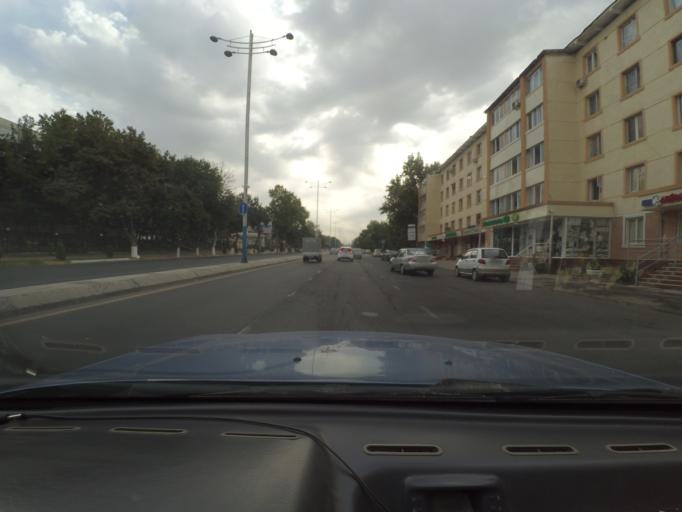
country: UZ
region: Toshkent
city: Salor
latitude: 41.3551
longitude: 69.3587
